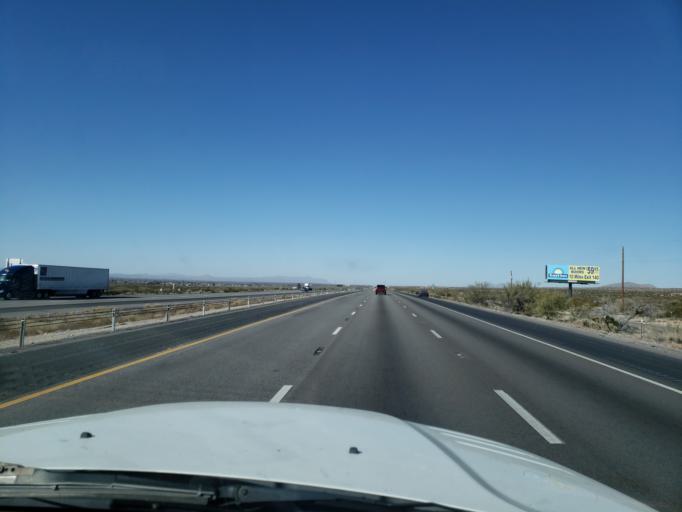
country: US
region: New Mexico
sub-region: Dona Ana County
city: Mesquite
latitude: 32.1890
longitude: -106.6804
